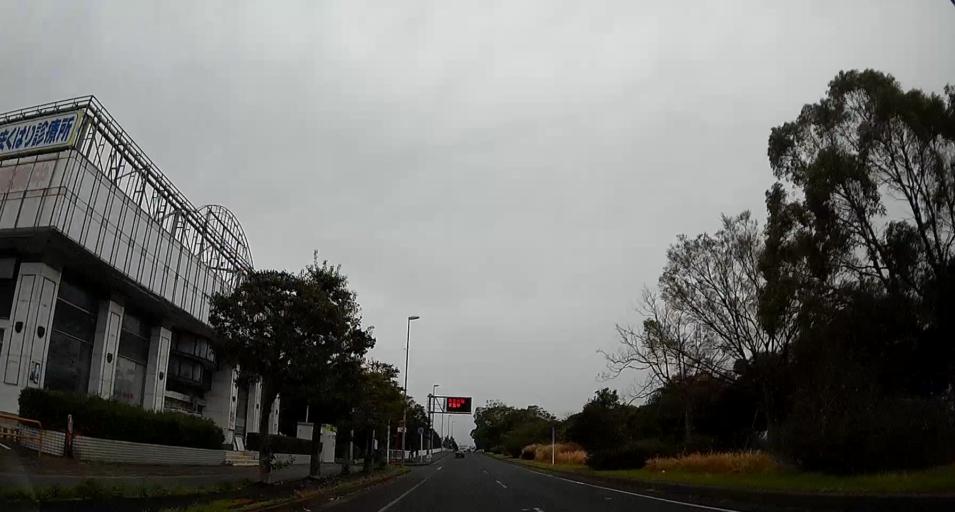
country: JP
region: Chiba
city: Chiba
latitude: 35.6522
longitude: 140.0591
